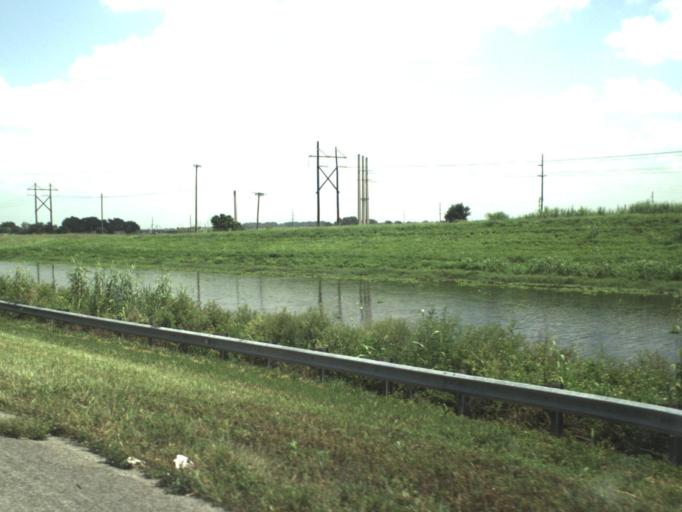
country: US
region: Florida
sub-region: Palm Beach County
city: South Bay
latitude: 26.6518
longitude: -80.7124
